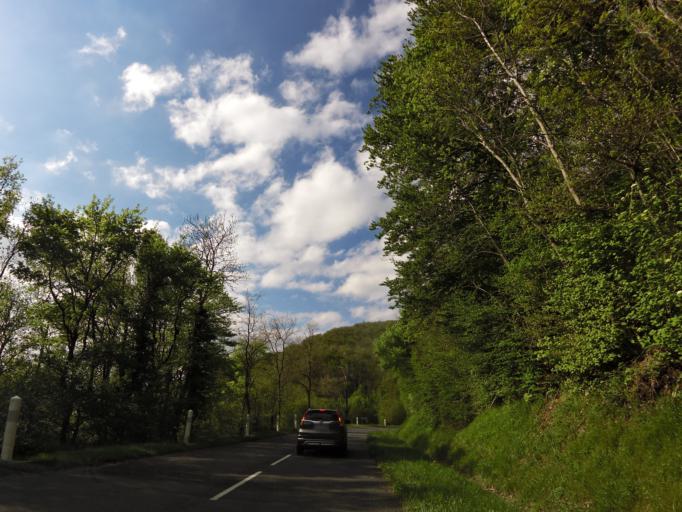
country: FR
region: Midi-Pyrenees
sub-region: Departement du Tarn
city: Soreze
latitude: 43.4298
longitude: 2.0546
